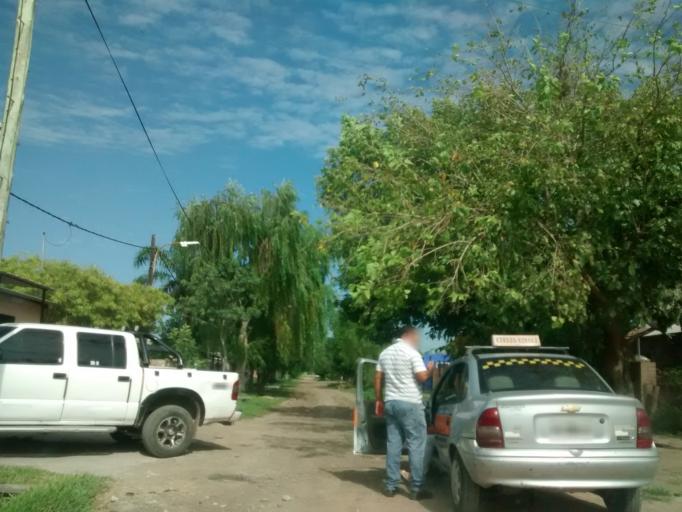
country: AR
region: Chaco
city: Fontana
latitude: -27.4000
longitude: -58.9910
